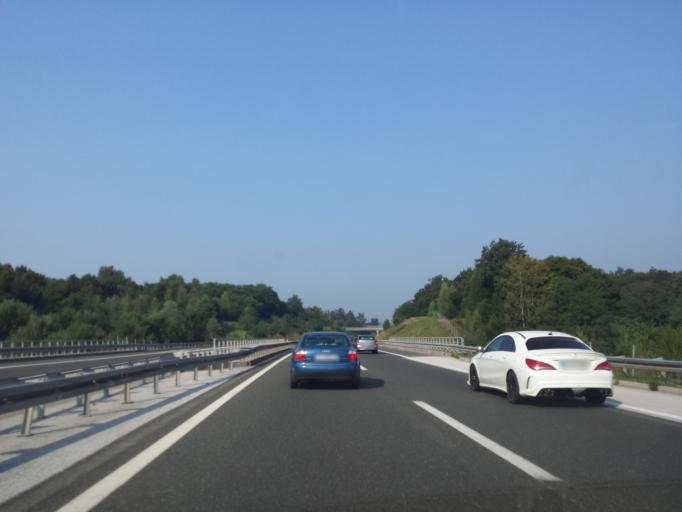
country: HR
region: Karlovacka
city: Ozalj
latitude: 45.4454
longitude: 15.3631
